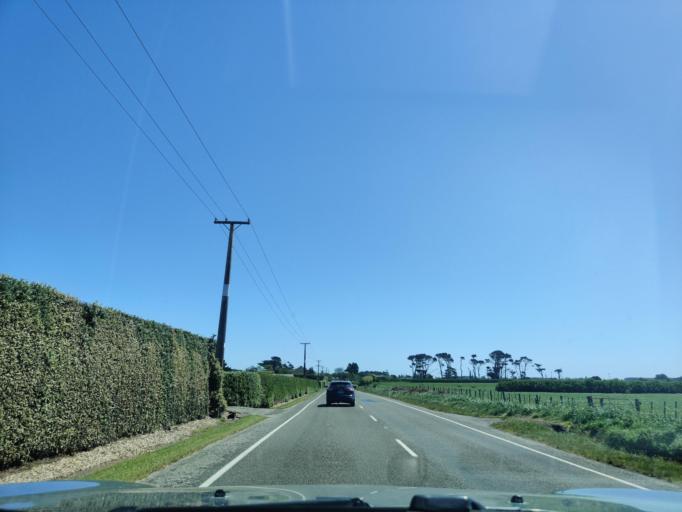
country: NZ
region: Taranaki
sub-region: South Taranaki District
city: Opunake
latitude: -39.5463
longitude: 174.0607
